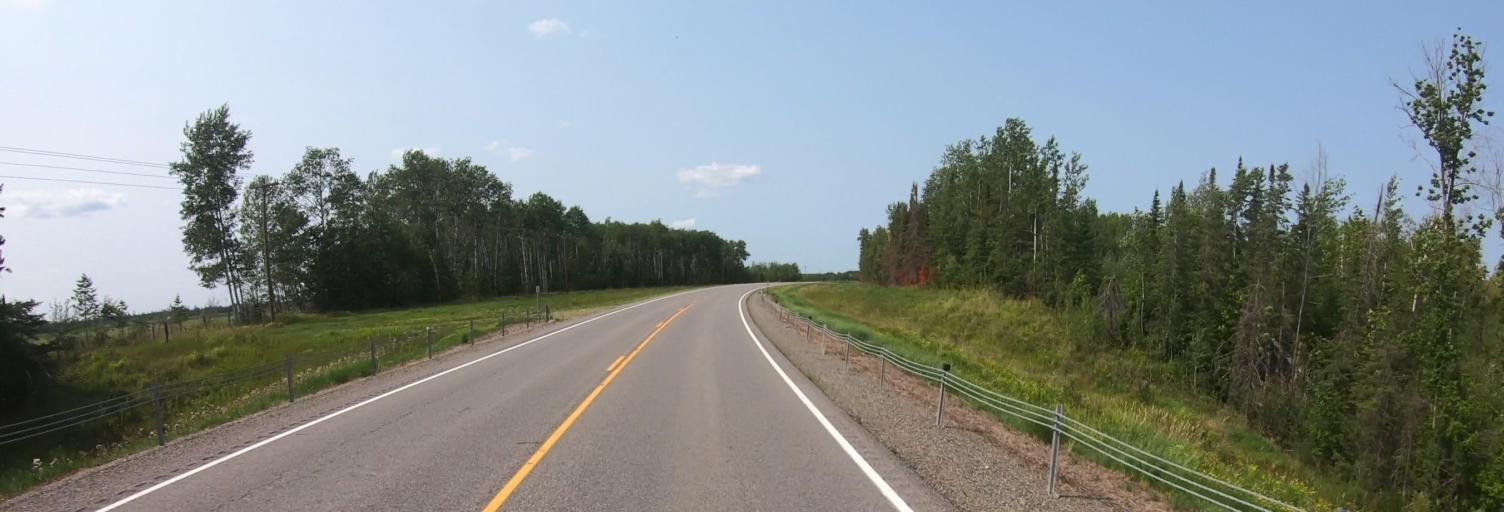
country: US
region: Minnesota
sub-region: Lake of the Woods County
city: Baudette
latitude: 48.6490
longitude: -94.2405
